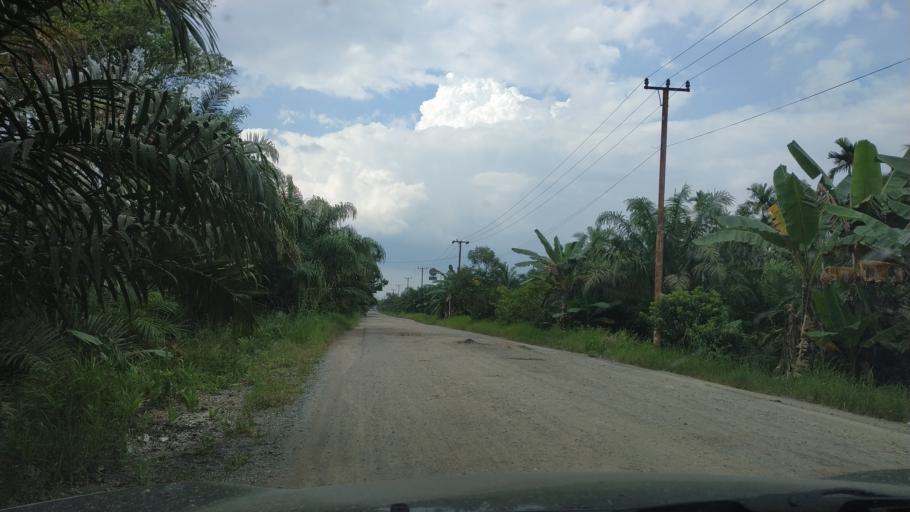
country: ID
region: Riau
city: Sungaisalak
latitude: -0.5246
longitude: 103.0043
